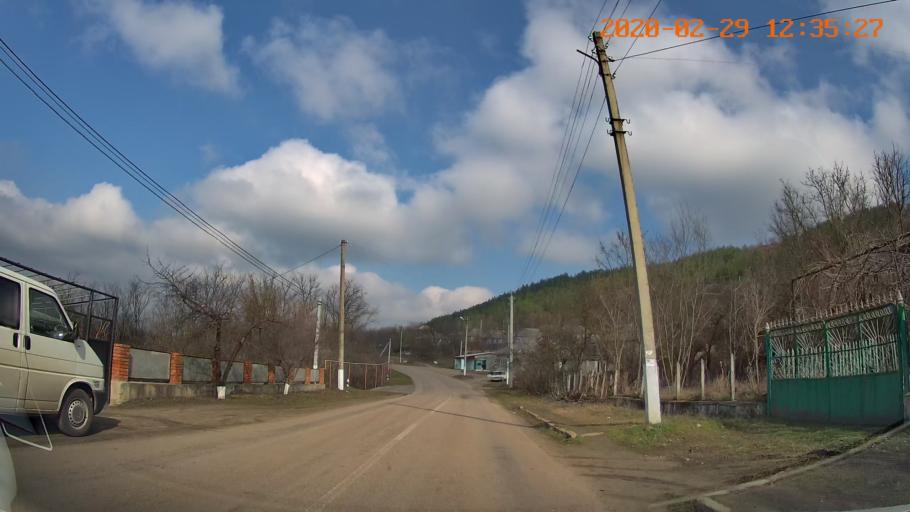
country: MD
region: Telenesti
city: Camenca
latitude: 48.0473
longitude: 28.7208
